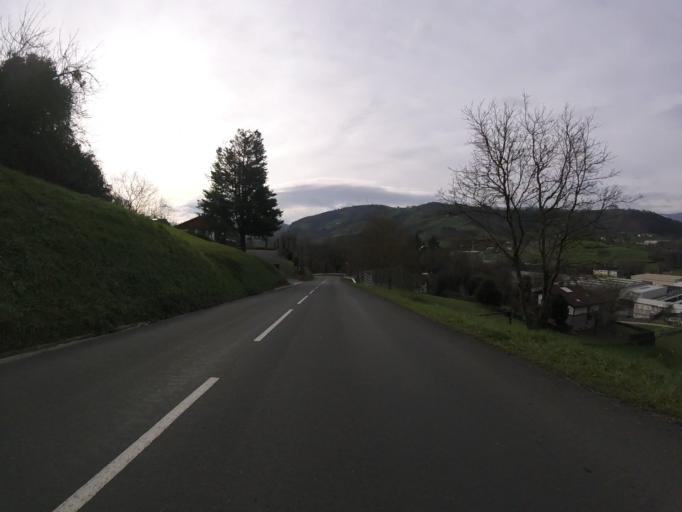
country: ES
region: Basque Country
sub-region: Provincia de Guipuzcoa
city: Azpeitia
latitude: 43.1745
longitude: -2.2490
